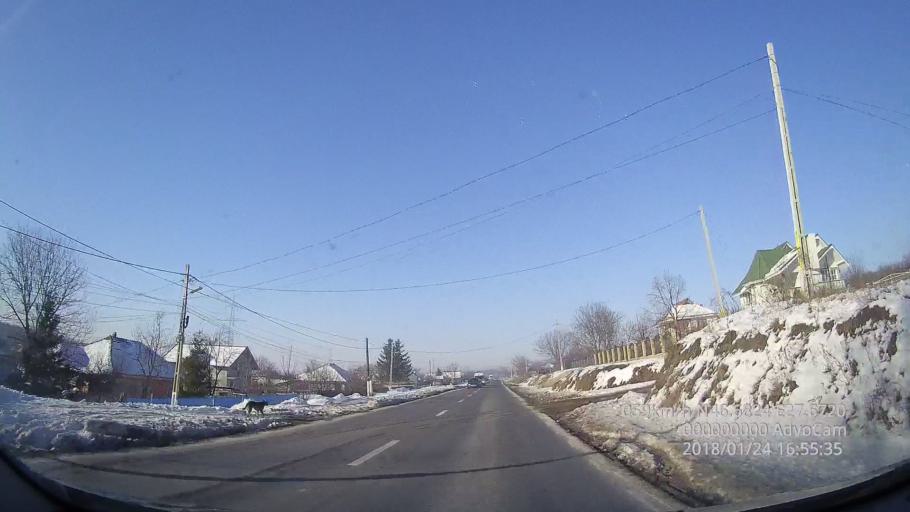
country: RO
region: Vaslui
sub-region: Municipiul Vaslui
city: Brodoc
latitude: 46.6827
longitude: 27.6719
